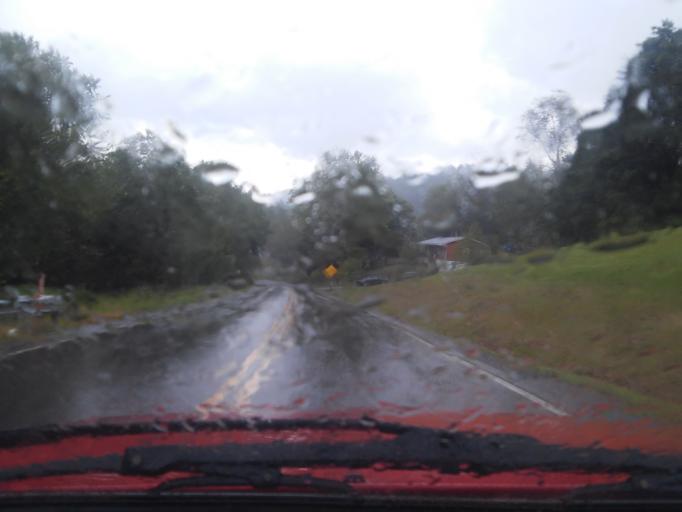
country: US
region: Virginia
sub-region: Montgomery County
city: Prices Fork
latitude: 37.2915
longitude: -80.4957
